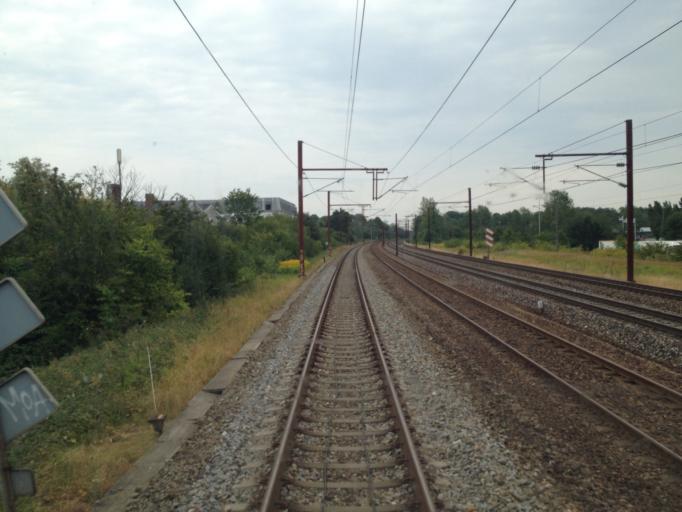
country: DK
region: Capital Region
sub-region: Glostrup Kommune
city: Glostrup
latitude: 55.6651
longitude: 12.4170
